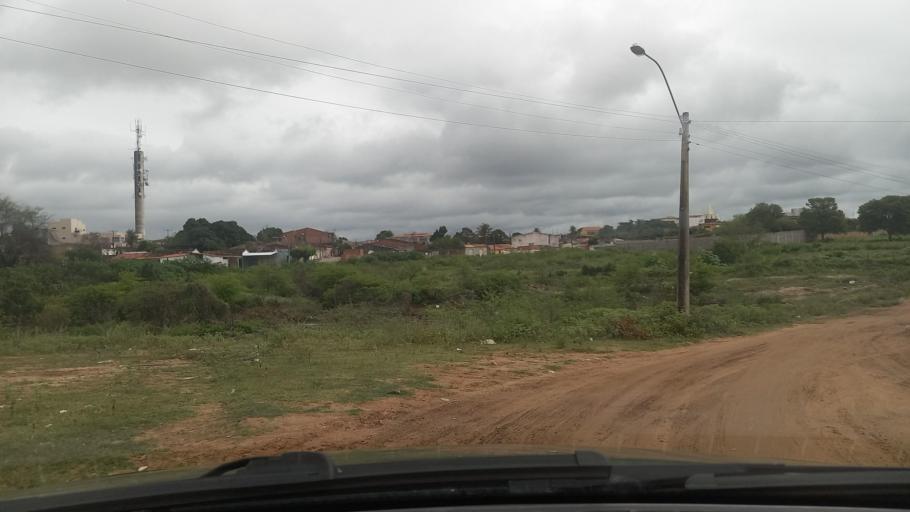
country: BR
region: Alagoas
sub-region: Delmiro Gouveia
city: Delmiro Gouveia
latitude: -9.3898
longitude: -37.9948
